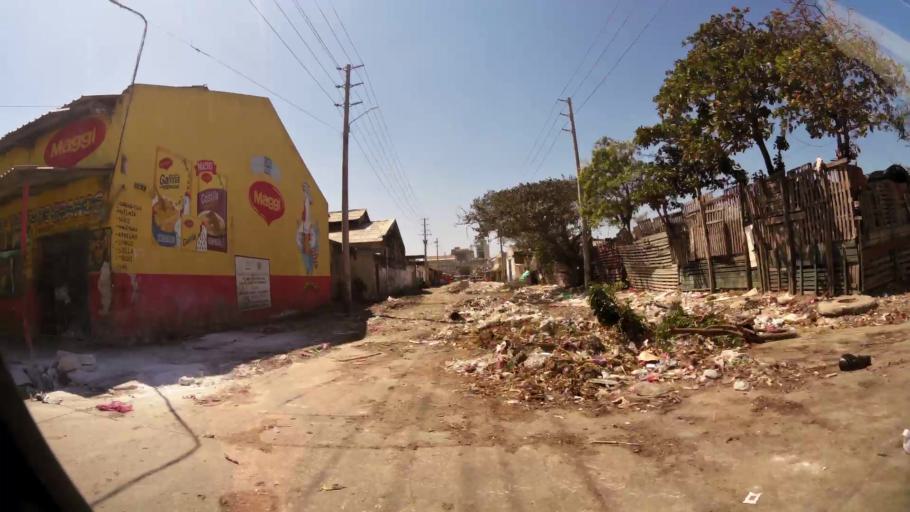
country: CO
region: Atlantico
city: Barranquilla
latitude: 10.9824
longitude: -74.7726
